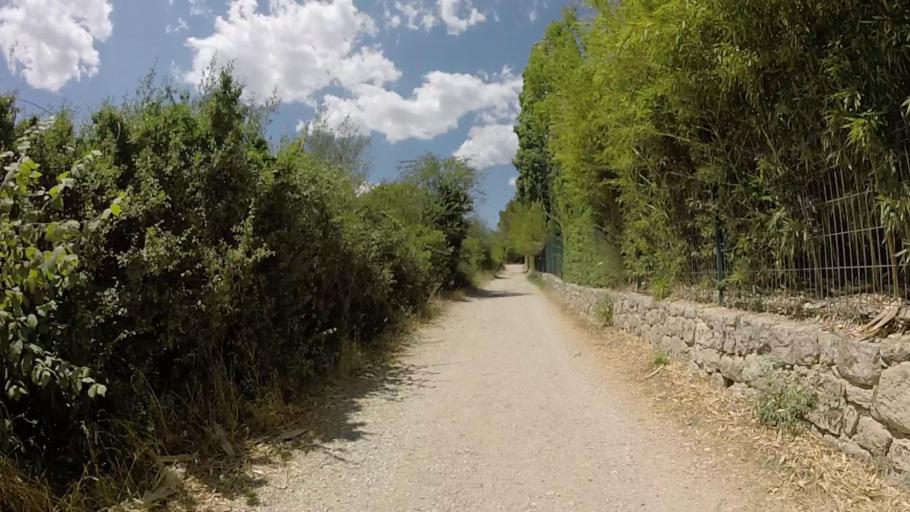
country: FR
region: Provence-Alpes-Cote d'Azur
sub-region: Departement des Alpes-Maritimes
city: Mougins
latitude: 43.5989
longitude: 7.0105
